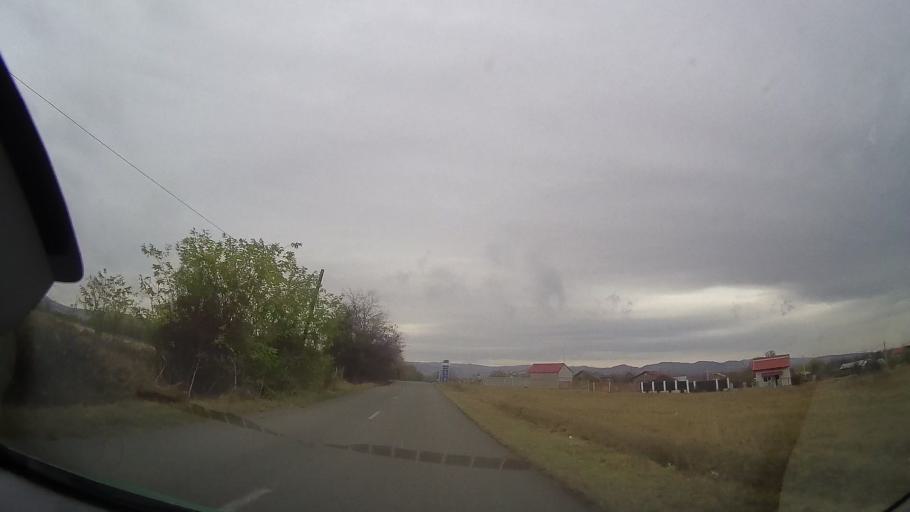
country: RO
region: Prahova
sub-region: Comuna Vadu Sapat
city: Vadu Sapat
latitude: 45.0269
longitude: 26.3835
